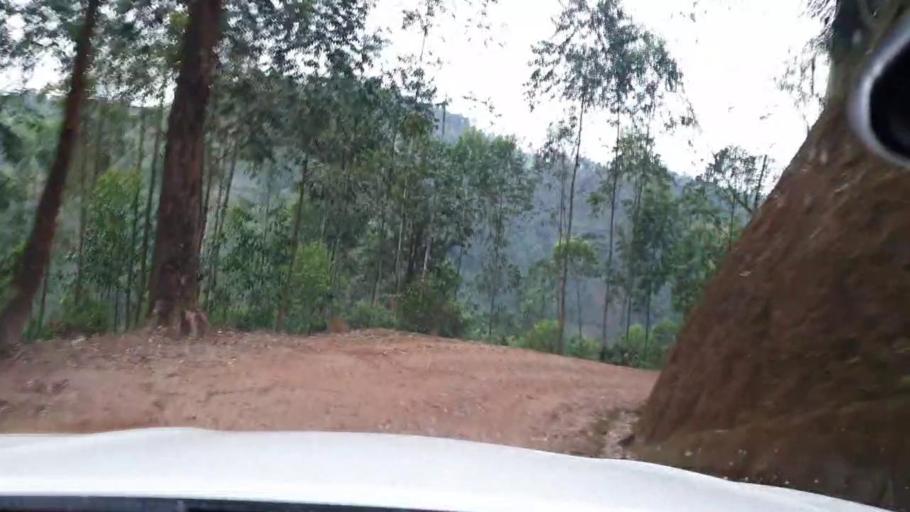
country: RW
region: Western Province
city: Cyangugu
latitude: -2.4131
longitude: 29.1966
